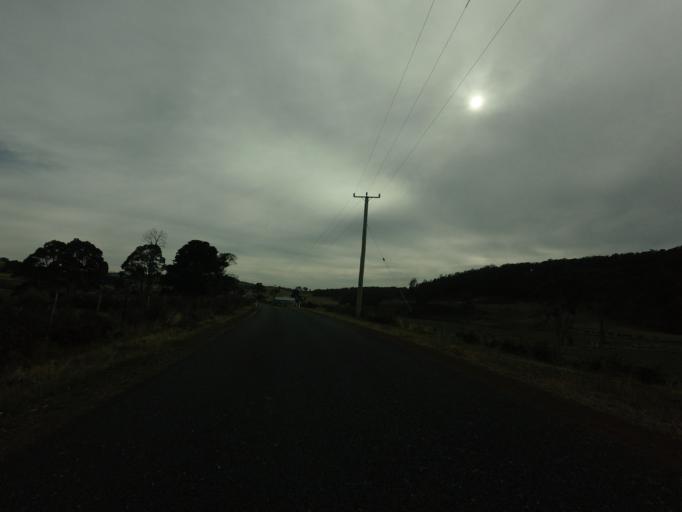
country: AU
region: Tasmania
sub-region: Sorell
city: Sorell
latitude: -42.4642
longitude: 147.5709
